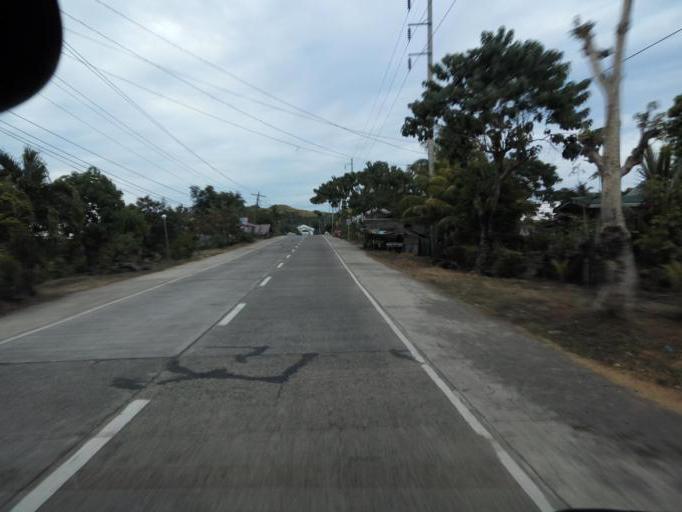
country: PH
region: Cagayan Valley
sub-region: Province of Cagayan
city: Casambalangan
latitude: 18.4069
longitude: 122.1307
